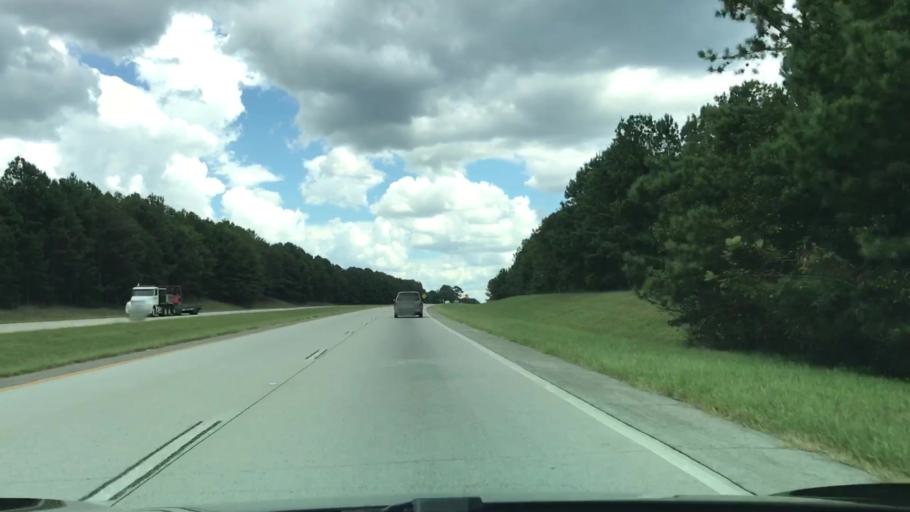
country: US
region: Georgia
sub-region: Barrow County
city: Statham
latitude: 33.9532
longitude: -83.5968
